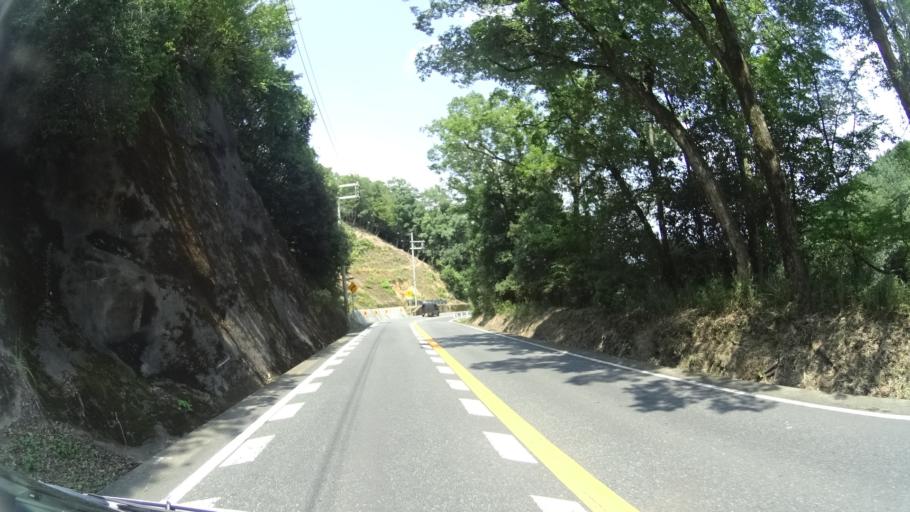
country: JP
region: Kyoto
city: Fukuchiyama
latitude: 35.2655
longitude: 135.1442
